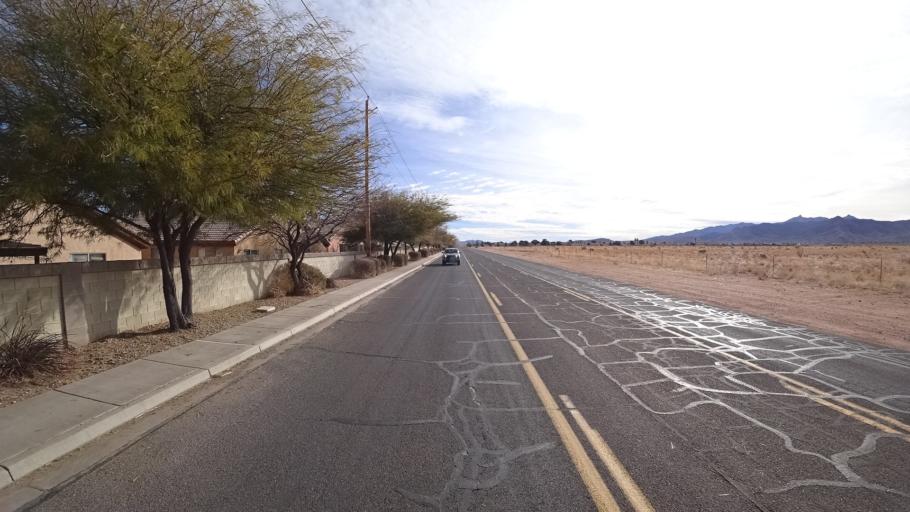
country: US
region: Arizona
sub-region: Mohave County
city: New Kingman-Butler
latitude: 35.2251
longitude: -113.9820
